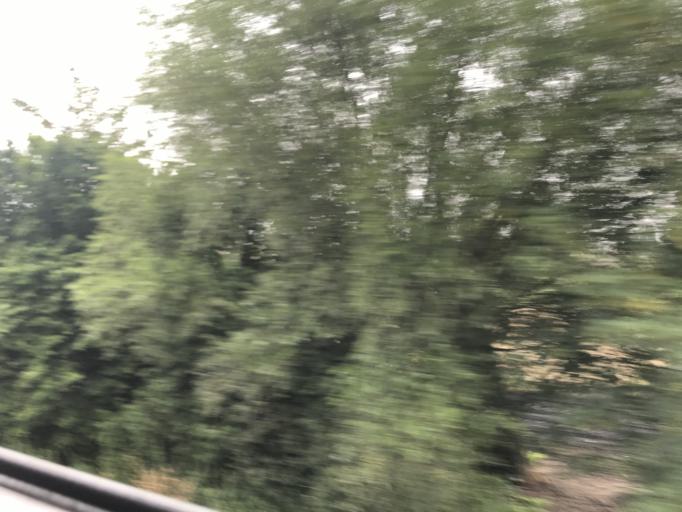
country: PL
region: Warmian-Masurian Voivodeship
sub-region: Powiat elblaski
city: Elblag
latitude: 54.1338
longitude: 19.3766
